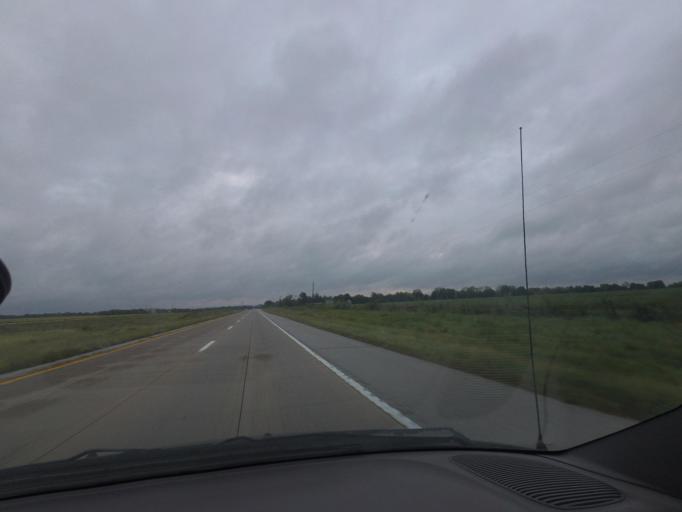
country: US
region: Missouri
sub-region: Marion County
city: Monroe City
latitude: 39.6580
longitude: -91.7671
